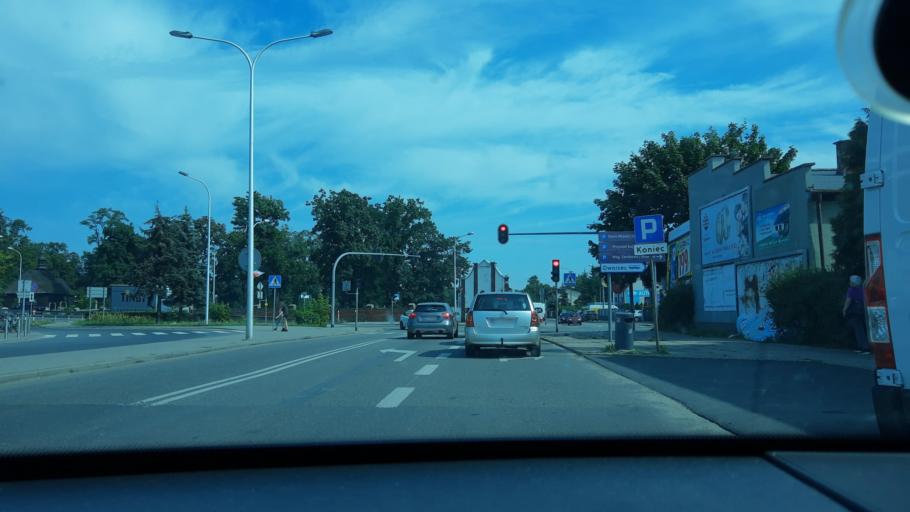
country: PL
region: Lodz Voivodeship
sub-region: Powiat sieradzki
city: Sieradz
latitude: 51.5970
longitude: 18.7269
